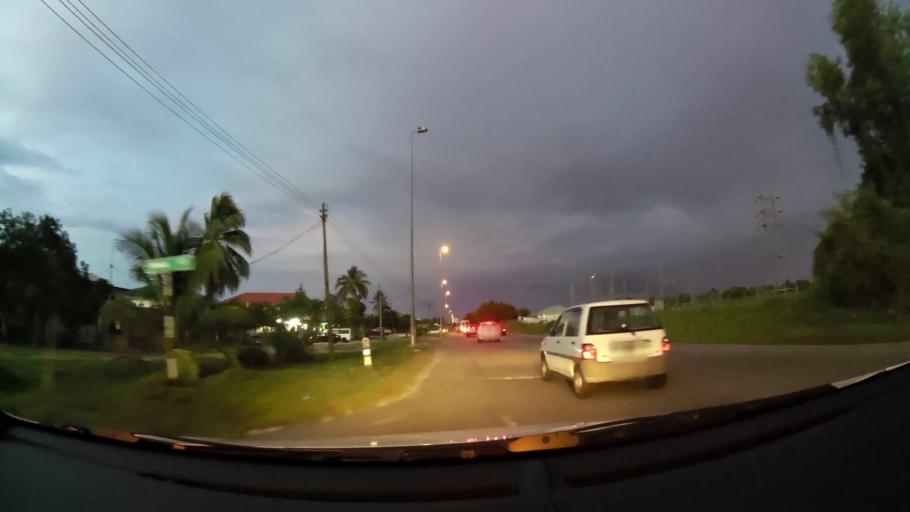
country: BN
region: Belait
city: Seria
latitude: 4.6503
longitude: 114.4196
